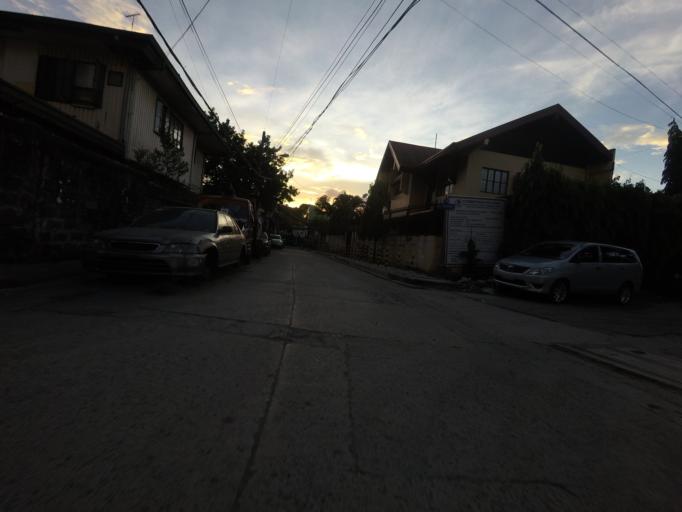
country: PH
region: Metro Manila
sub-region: San Juan
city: San Juan
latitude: 14.6016
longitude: 121.0334
